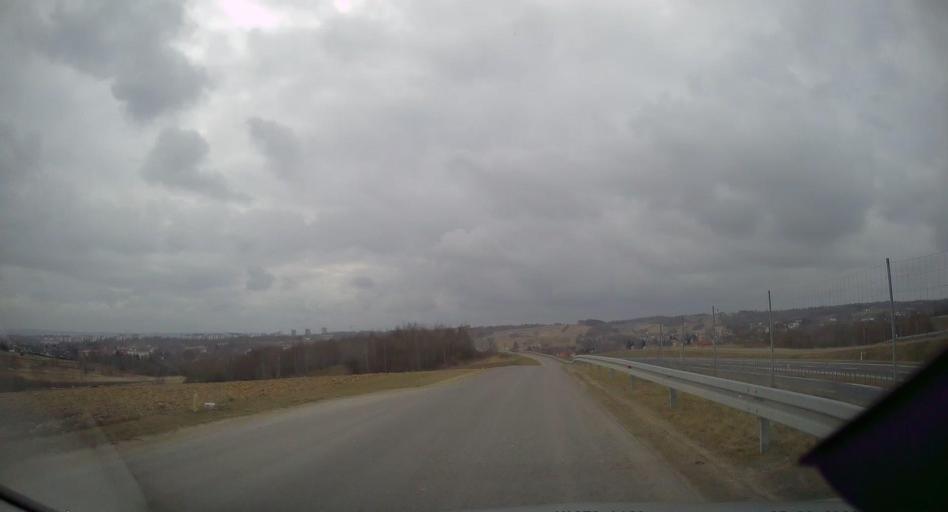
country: PL
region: Subcarpathian Voivodeship
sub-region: Rzeszow
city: Przybyszowka
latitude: 50.0545
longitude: 21.9250
